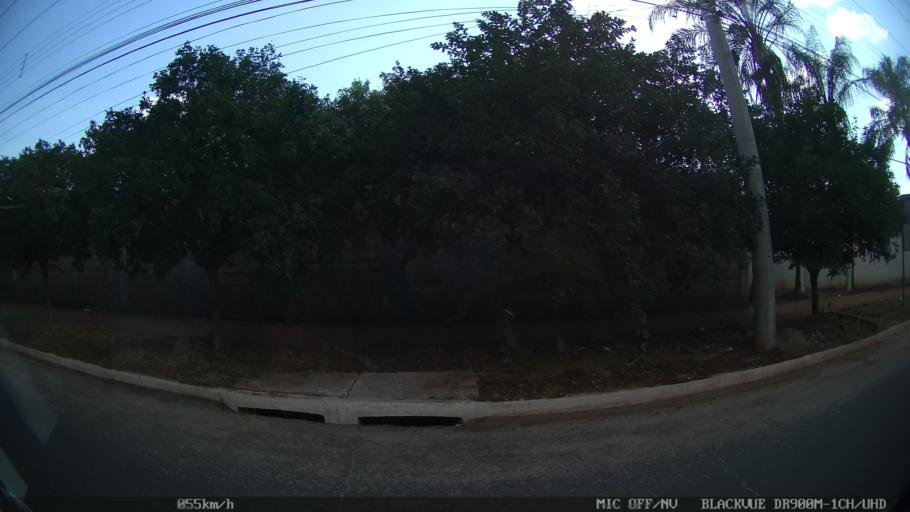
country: BR
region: Sao Paulo
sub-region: Ribeirao Preto
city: Ribeirao Preto
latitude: -21.1823
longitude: -47.8413
